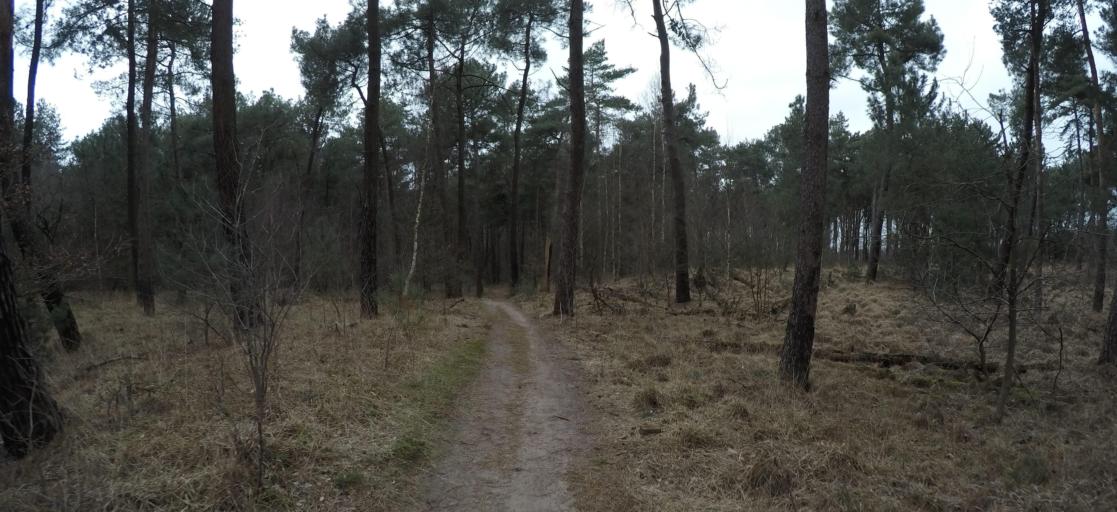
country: BE
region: Flanders
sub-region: Provincie Antwerpen
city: Kalmthout
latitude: 51.4170
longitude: 4.4110
